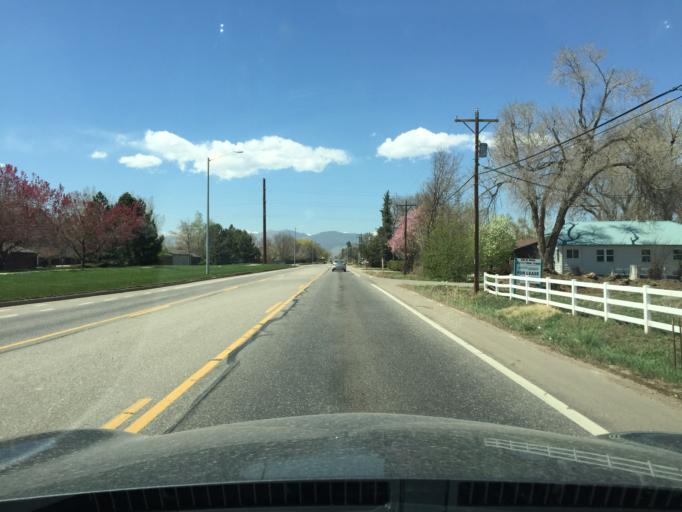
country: US
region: Colorado
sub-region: Boulder County
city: Longmont
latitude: 40.1525
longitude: -105.1381
